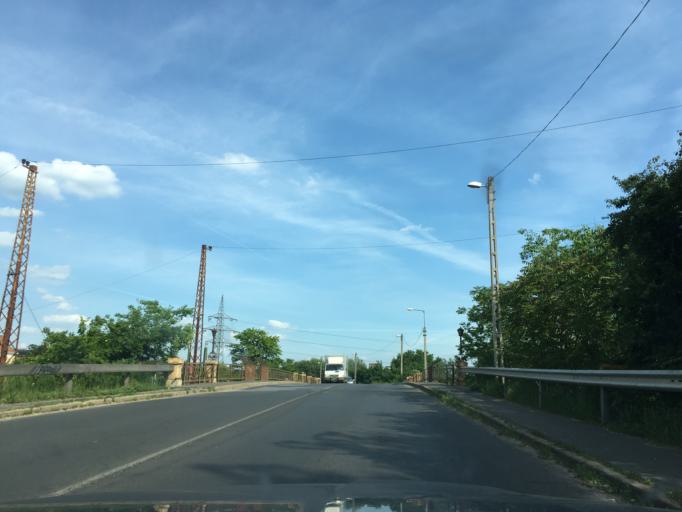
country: HU
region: Hajdu-Bihar
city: Debrecen
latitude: 47.5252
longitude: 21.6406
